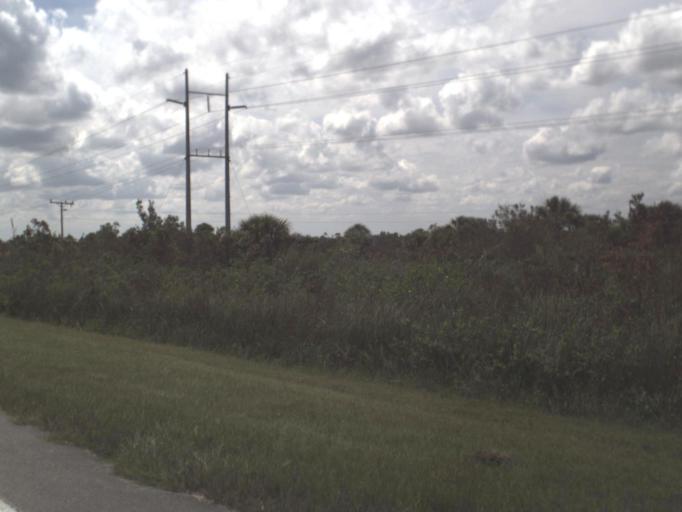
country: US
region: Florida
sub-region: Collier County
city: Orangetree
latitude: 26.1378
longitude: -81.3450
